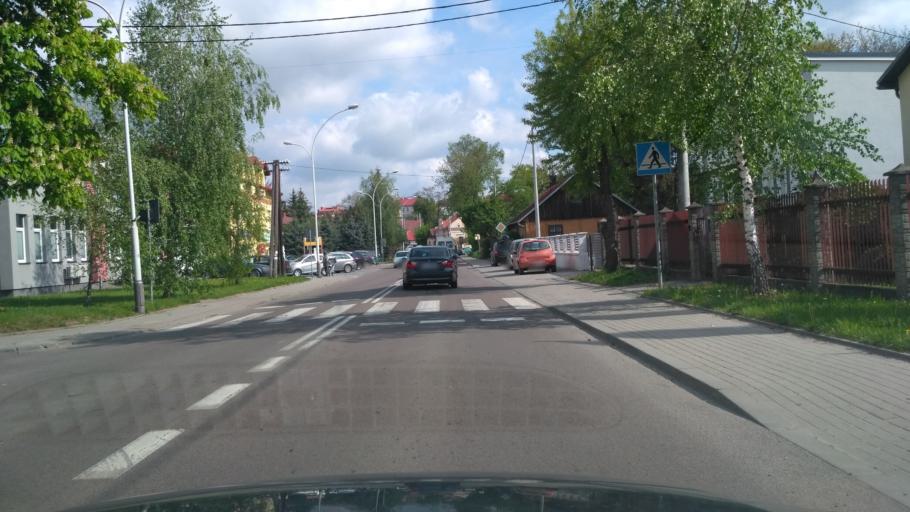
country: PL
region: Subcarpathian Voivodeship
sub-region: Powiat przeworski
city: Przeworsk
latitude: 50.0532
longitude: 22.4921
